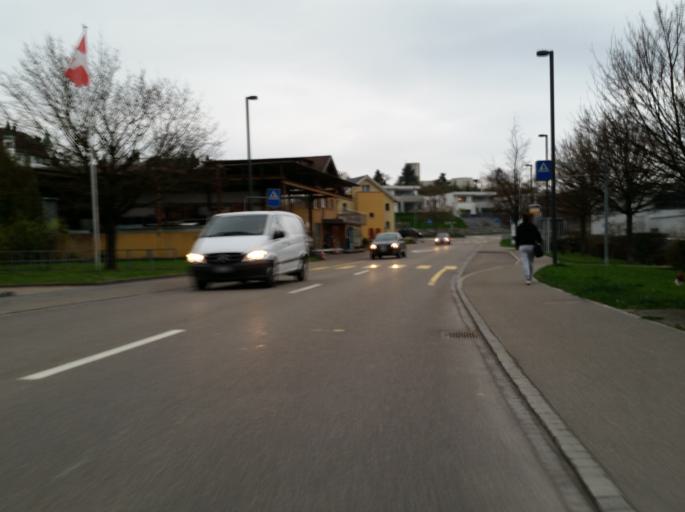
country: CH
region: Appenzell Ausserrhoden
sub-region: Bezirk Vorderland
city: Heiden
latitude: 47.4774
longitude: 9.5429
